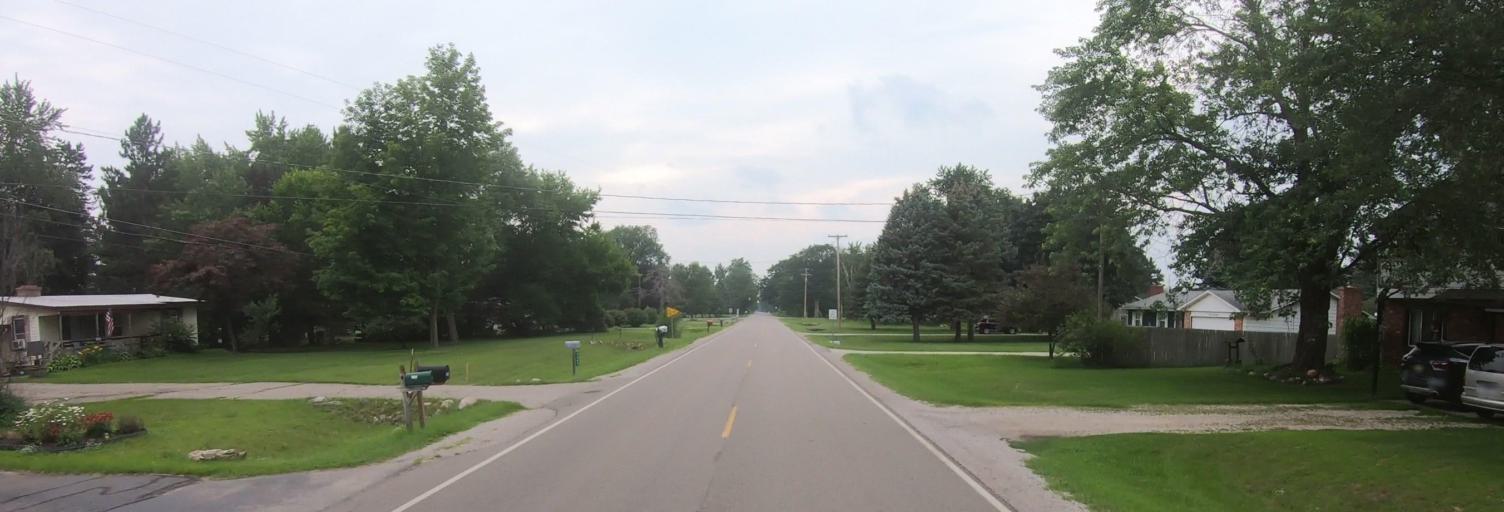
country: US
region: Michigan
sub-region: Genesee County
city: Clio
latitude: 43.1339
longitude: -83.7909
